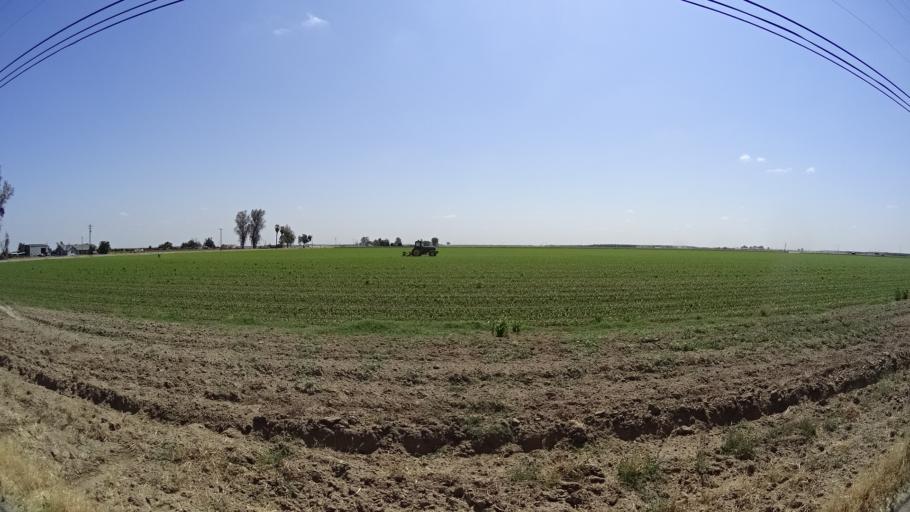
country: US
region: California
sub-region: Kings County
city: Home Garden
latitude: 36.2682
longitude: -119.6191
